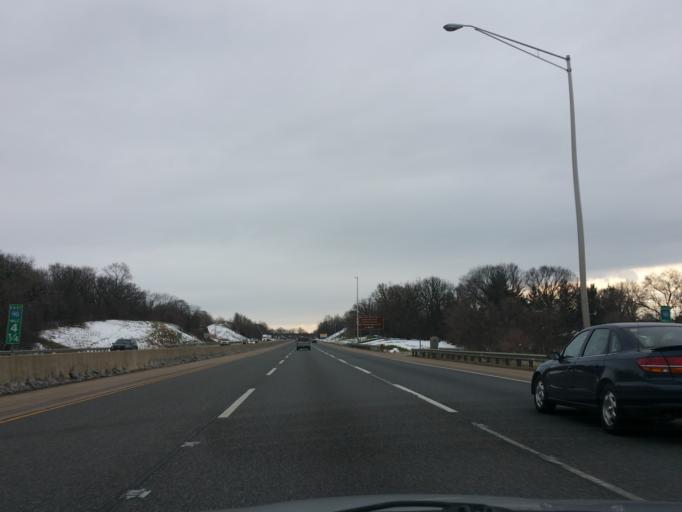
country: US
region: Illinois
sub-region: Winnebago County
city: Roscoe
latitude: 42.4351
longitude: -88.9891
